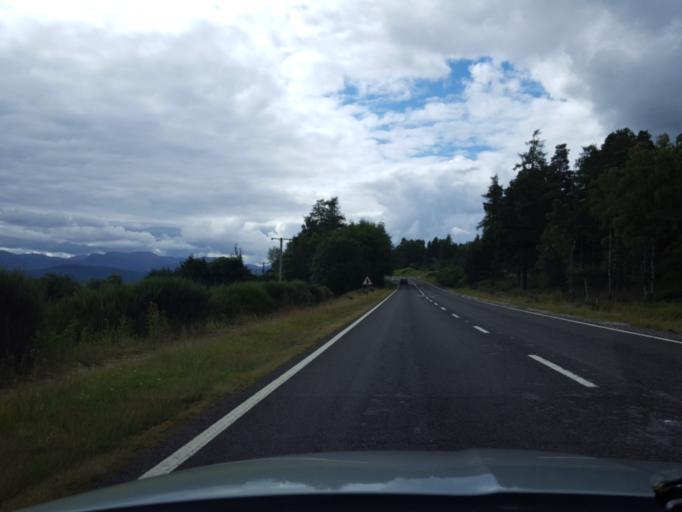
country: GB
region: Scotland
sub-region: Highland
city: Grantown on Spey
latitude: 57.2929
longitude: -3.6651
